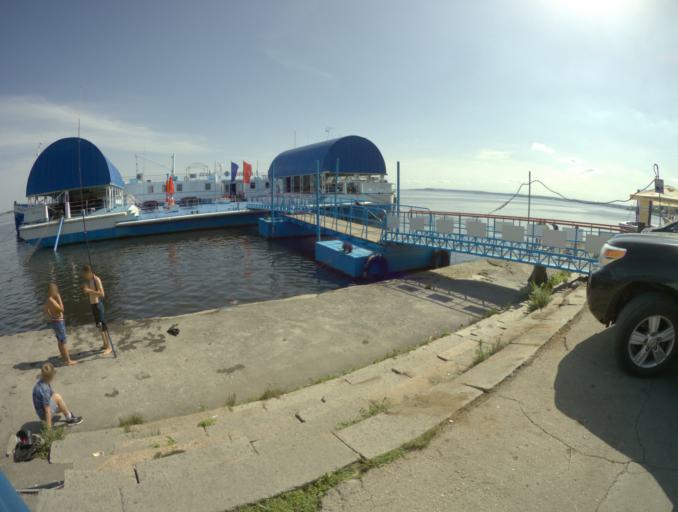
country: RU
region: Saratov
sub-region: Saratovskiy Rayon
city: Saratov
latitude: 51.5245
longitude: 46.0476
